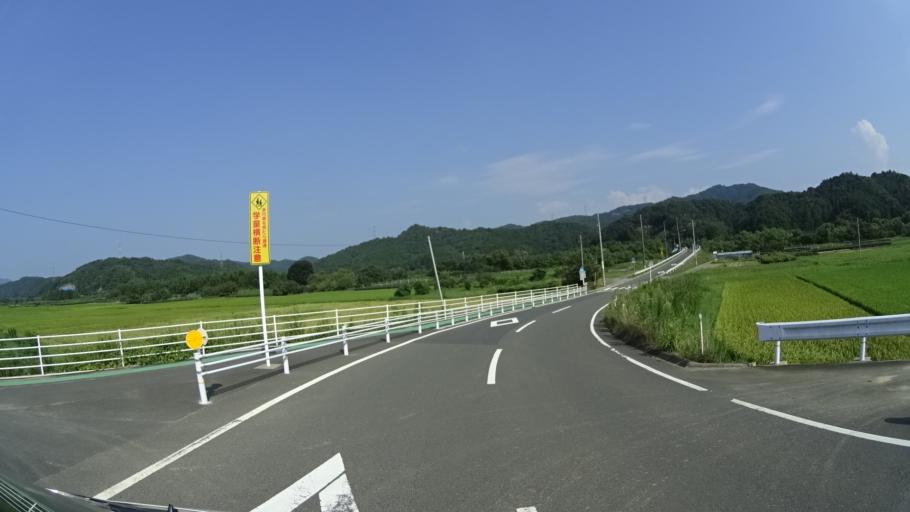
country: JP
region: Kyoto
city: Maizuru
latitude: 35.4303
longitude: 135.2521
